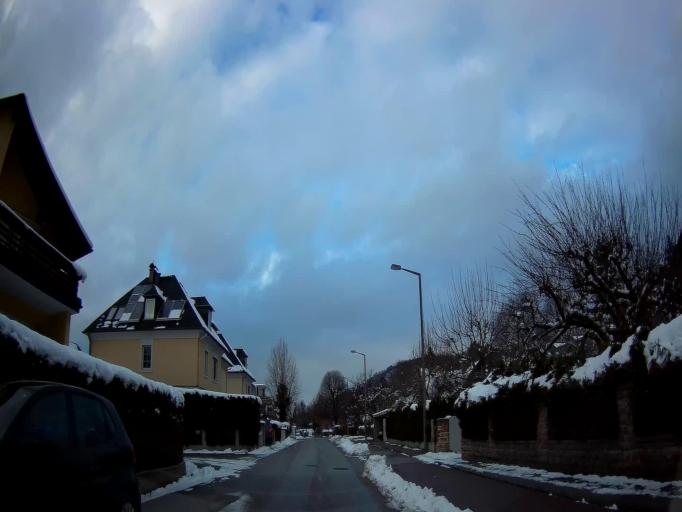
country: AT
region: Salzburg
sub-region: Salzburg Stadt
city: Salzburg
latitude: 47.7905
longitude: 13.0834
